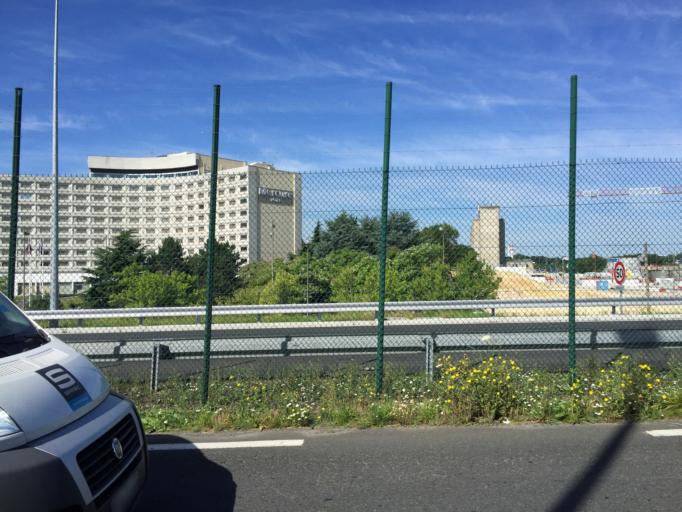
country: FR
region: Ile-de-France
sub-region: Departement du Val-d'Oise
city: Roissy-en-France
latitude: 49.0082
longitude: 2.5507
